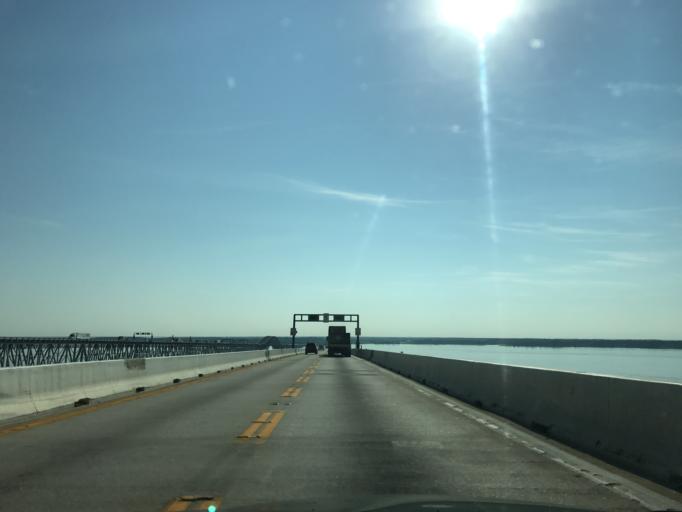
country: US
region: Maryland
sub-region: Queen Anne's County
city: Stevensville
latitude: 38.9912
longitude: -76.3734
